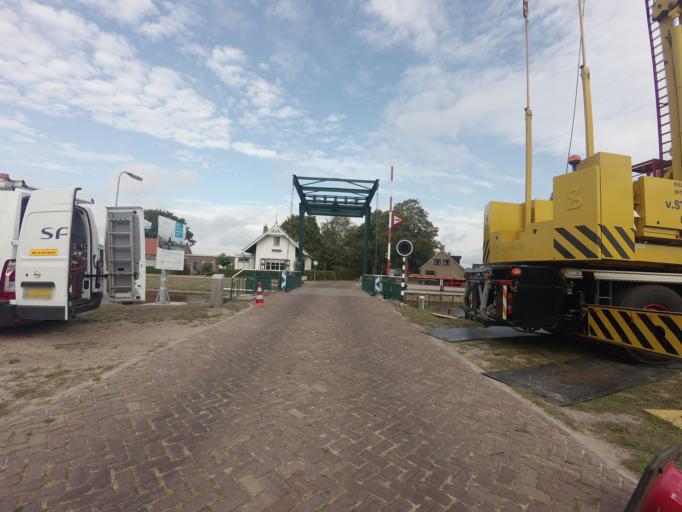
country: NL
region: Friesland
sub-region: Gemeente Heerenveen
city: Jubbega
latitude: 52.9721
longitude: 6.1515
